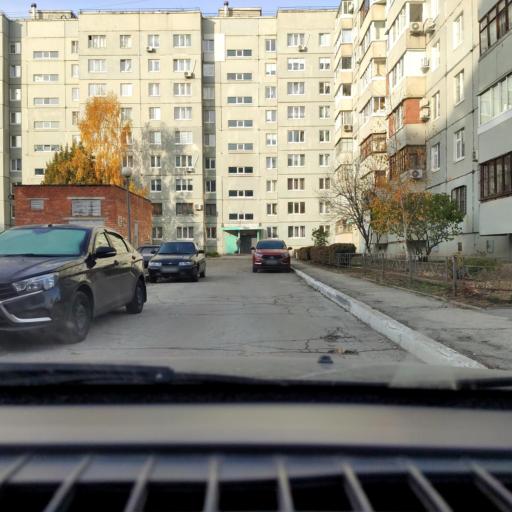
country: RU
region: Samara
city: Tol'yatti
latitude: 53.5413
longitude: 49.3590
